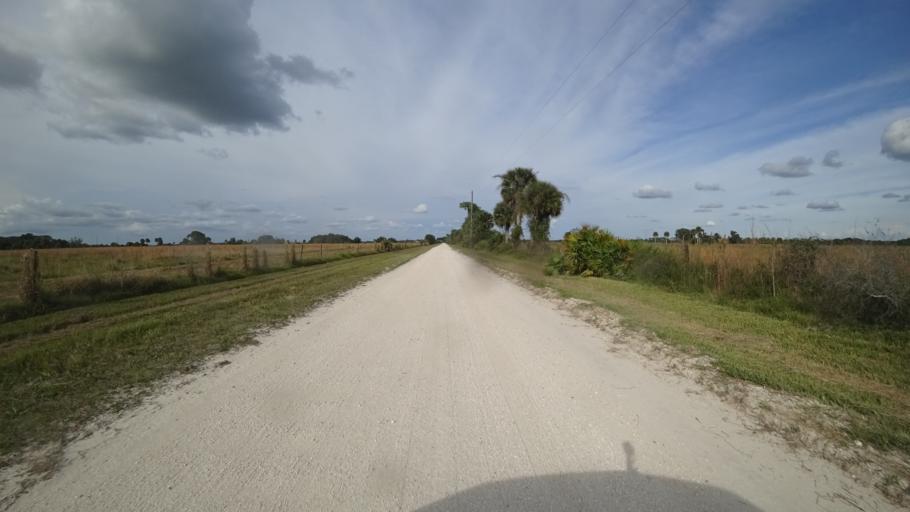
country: US
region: Florida
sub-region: Sarasota County
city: Warm Mineral Springs
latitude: 27.2463
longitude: -82.1658
